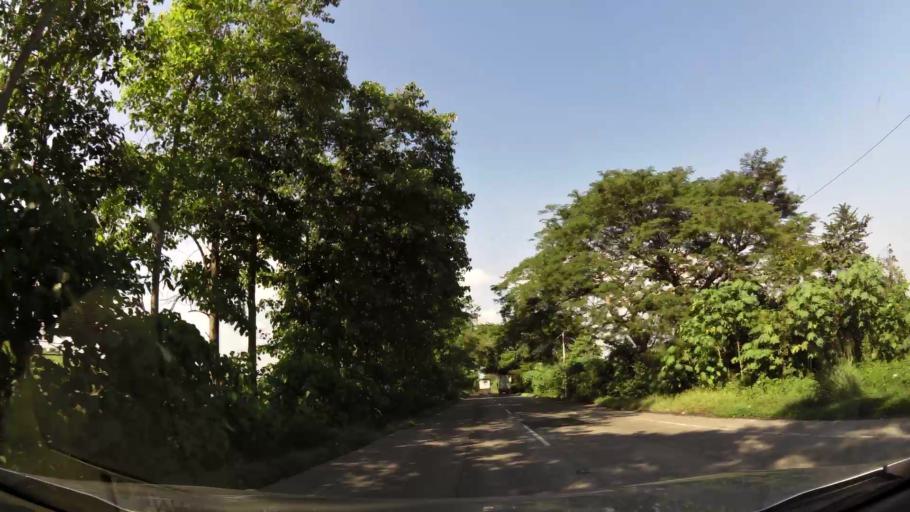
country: GT
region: Escuintla
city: Puerto San Jose
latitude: 13.9906
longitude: -90.7883
